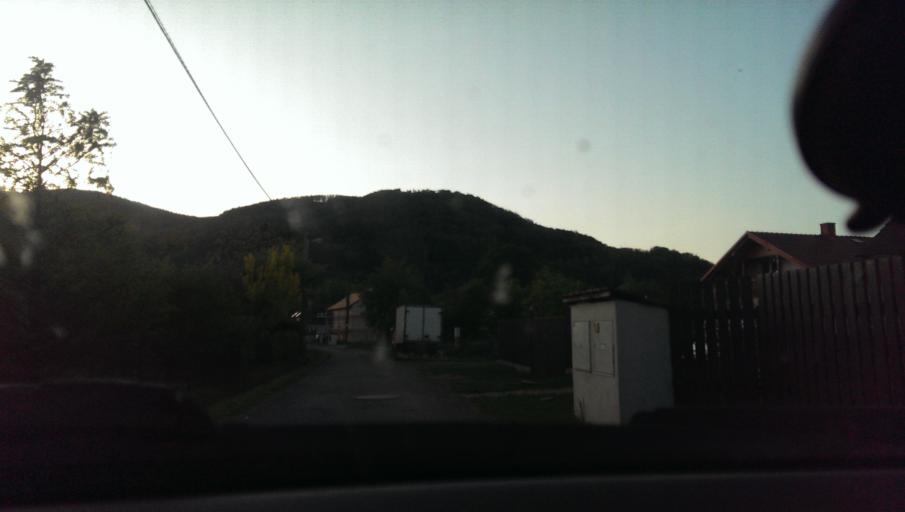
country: CZ
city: Lichnov (o. Novy Jicin)
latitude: 49.5691
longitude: 18.1824
